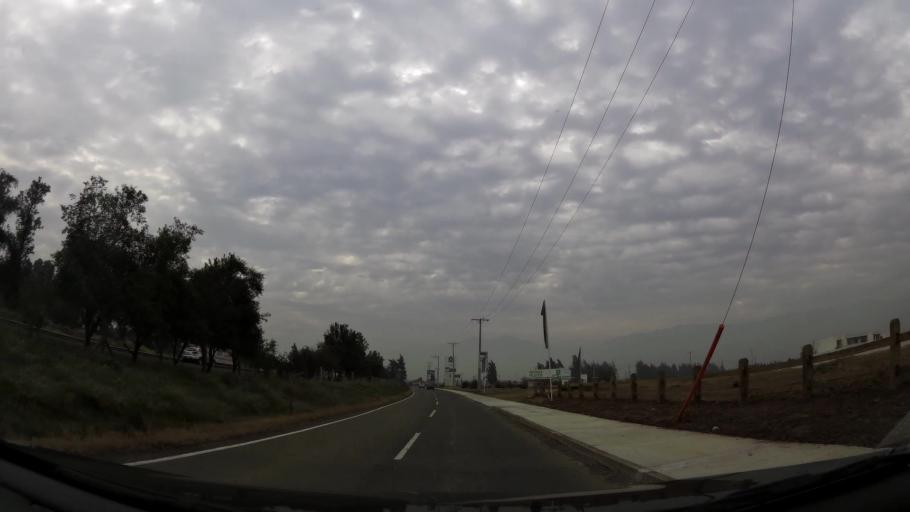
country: CL
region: Santiago Metropolitan
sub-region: Provincia de Chacabuco
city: Chicureo Abajo
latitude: -33.2286
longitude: -70.6855
